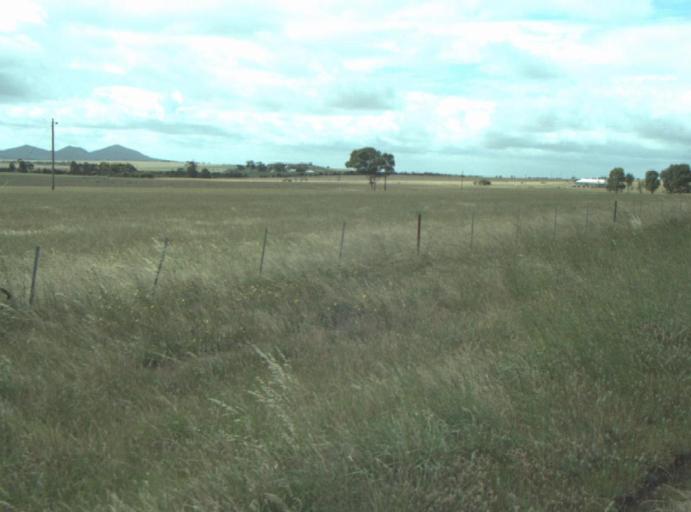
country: AU
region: Victoria
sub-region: Greater Geelong
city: Lara
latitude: -37.8623
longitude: 144.3248
